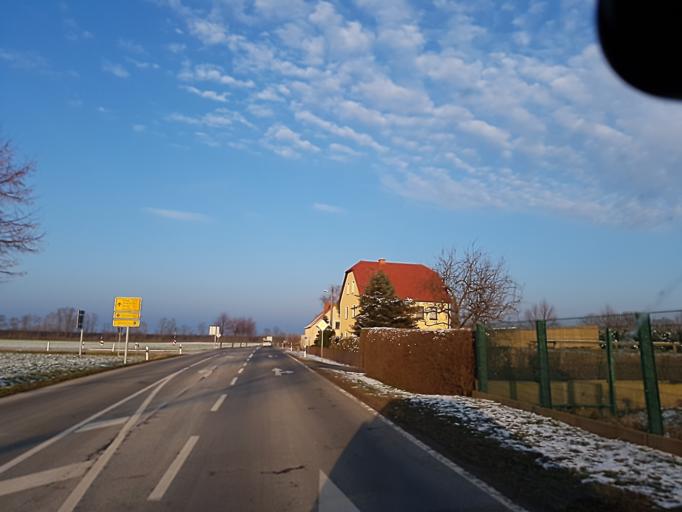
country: DE
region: Saxony
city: Oschatz
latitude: 51.2990
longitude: 13.1611
